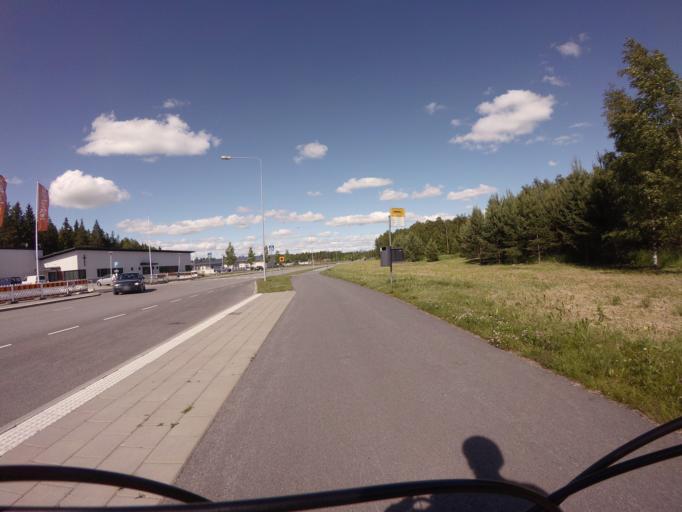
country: FI
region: Varsinais-Suomi
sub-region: Turku
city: Vahto
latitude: 60.5345
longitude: 22.3069
